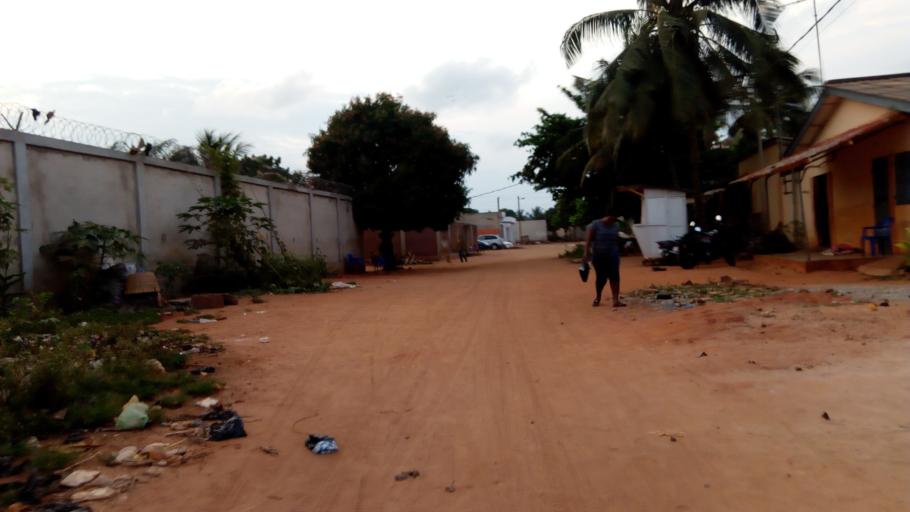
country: TG
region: Maritime
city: Lome
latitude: 6.2308
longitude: 1.1849
